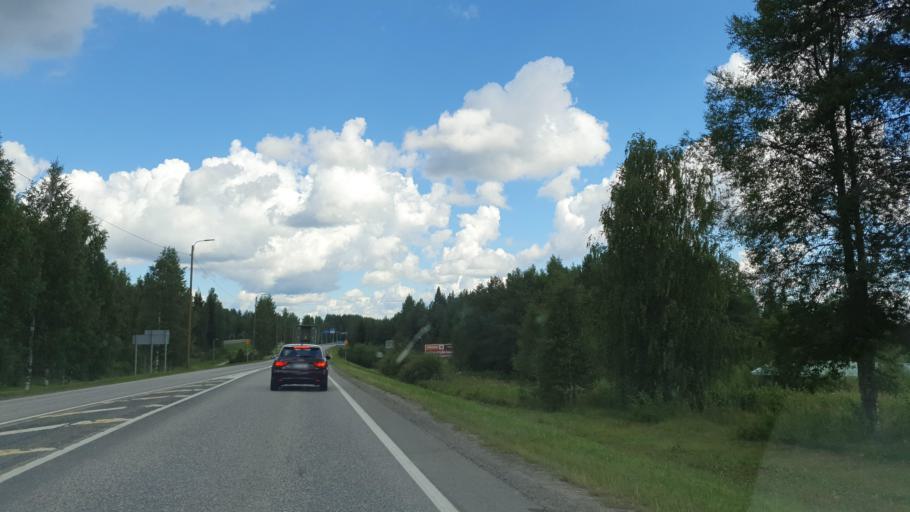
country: FI
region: Kainuu
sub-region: Kajaani
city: Kajaani
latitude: 64.2115
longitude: 27.6598
